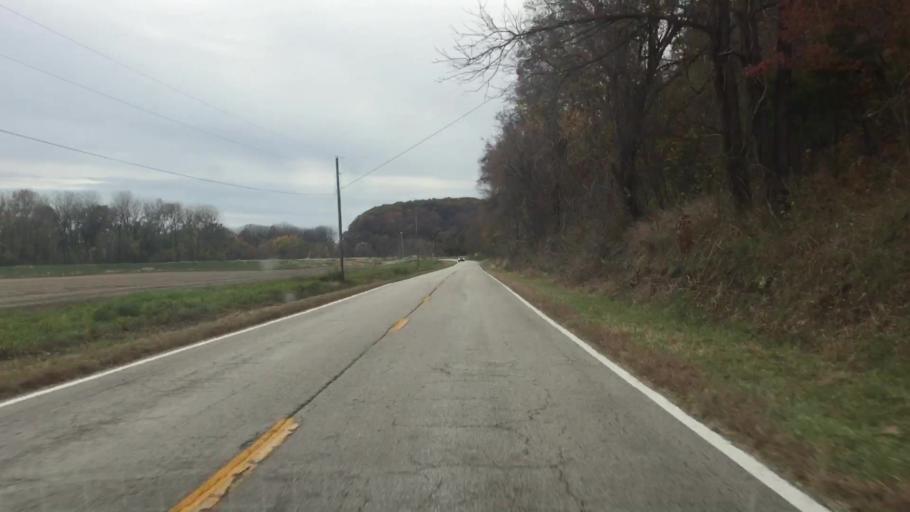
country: US
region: Missouri
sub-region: Gasconade County
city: Hermann
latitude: 38.7048
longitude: -91.6175
